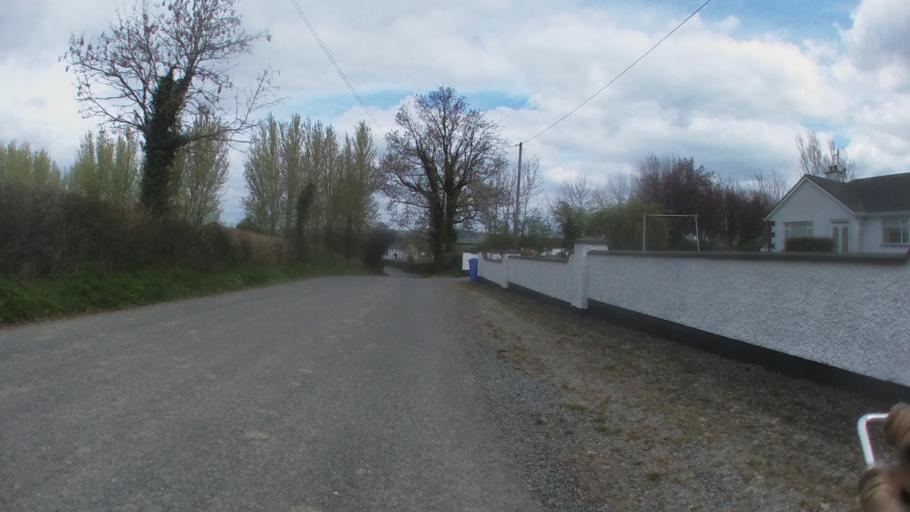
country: IE
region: Leinster
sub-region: Kilkenny
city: Kilkenny
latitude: 52.6519
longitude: -7.1841
